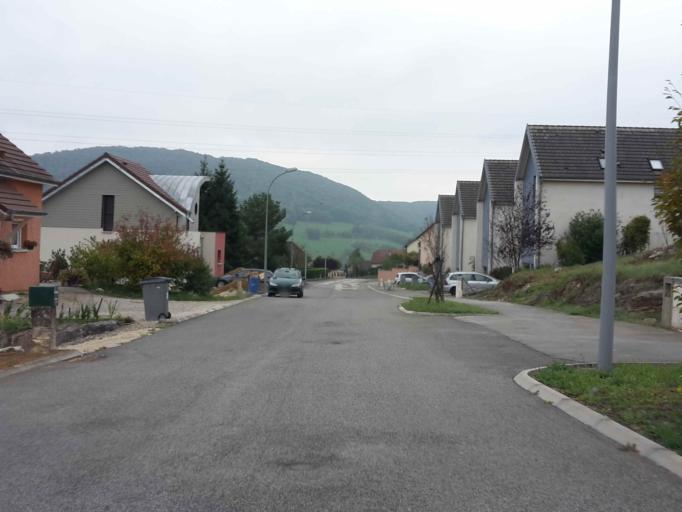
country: FR
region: Franche-Comte
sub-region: Departement du Doubs
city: Baume-les-Dames
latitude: 47.3526
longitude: 6.3369
